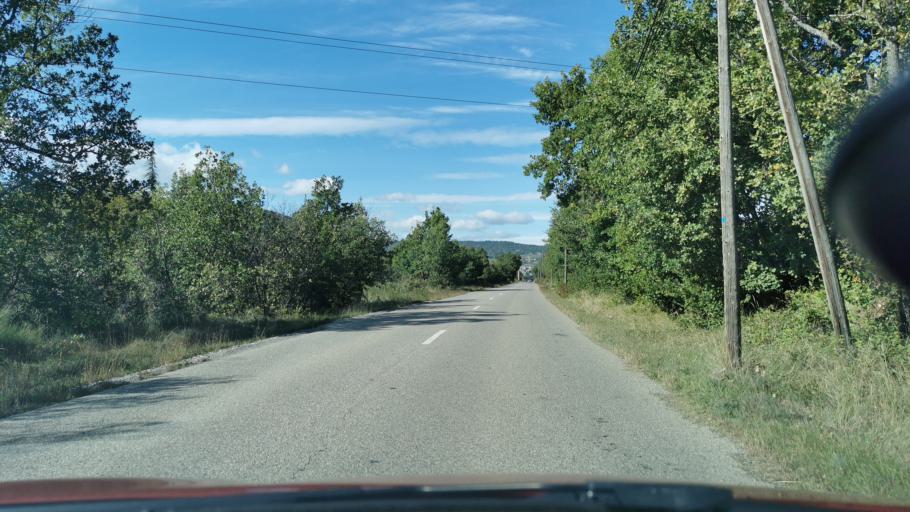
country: FR
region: Provence-Alpes-Cote d'Azur
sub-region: Departement des Alpes-de-Haute-Provence
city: Peipin
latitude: 44.1613
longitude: 5.9655
